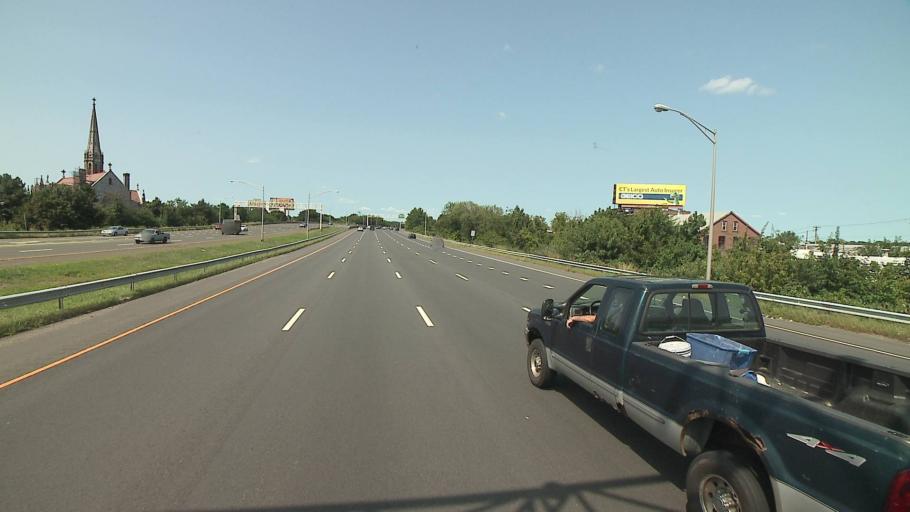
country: US
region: Connecticut
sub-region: Fairfield County
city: Bridgeport
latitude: 41.1914
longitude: -73.1942
